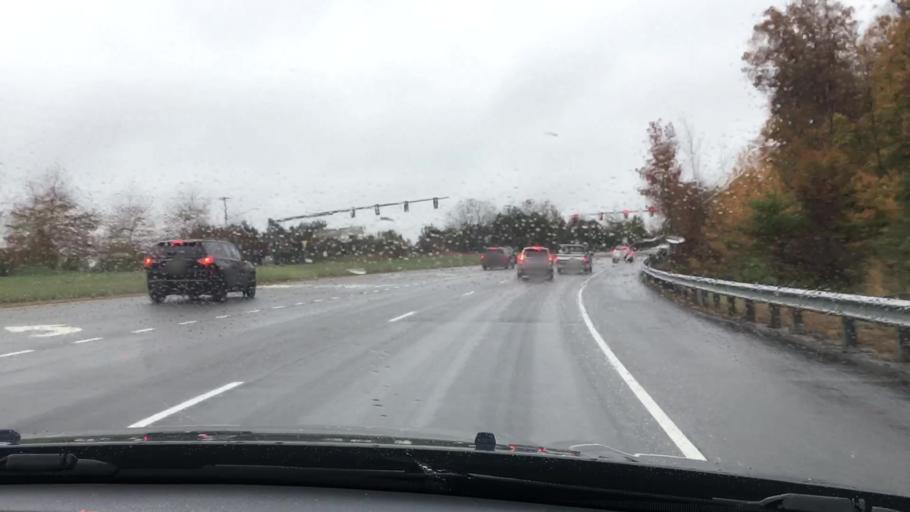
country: US
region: Virginia
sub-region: Prince William County
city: Lake Ridge
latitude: 38.7361
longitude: -77.2807
